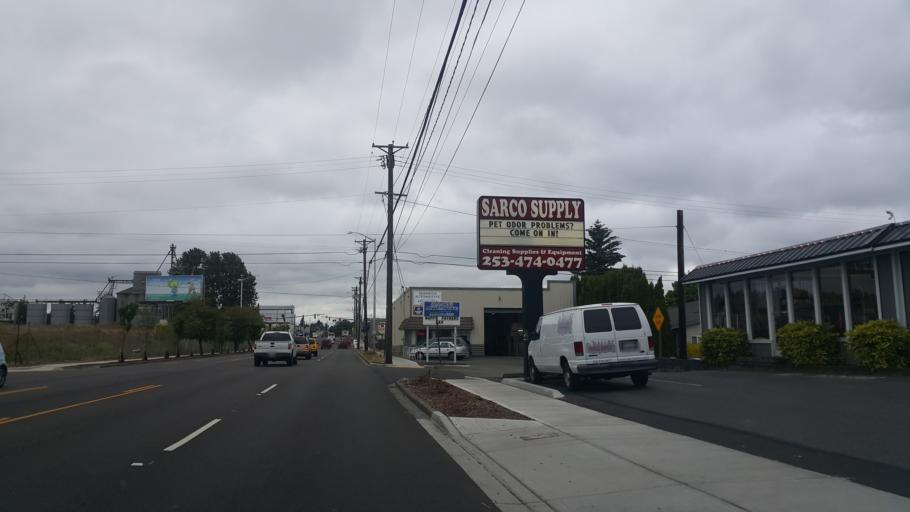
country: US
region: Washington
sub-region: Pierce County
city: Fircrest
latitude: 47.2061
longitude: -122.4896
